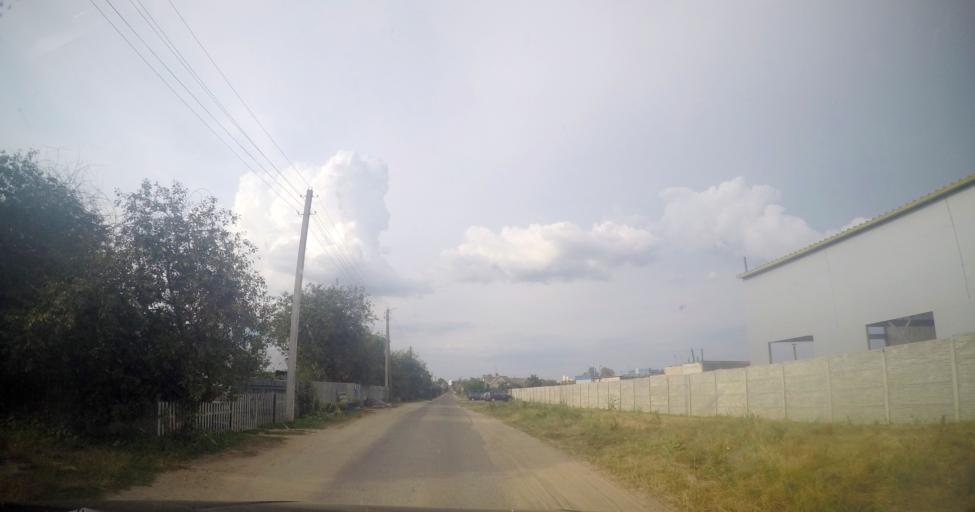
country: BY
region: Grodnenskaya
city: Hrodna
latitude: 53.6237
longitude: 23.8370
